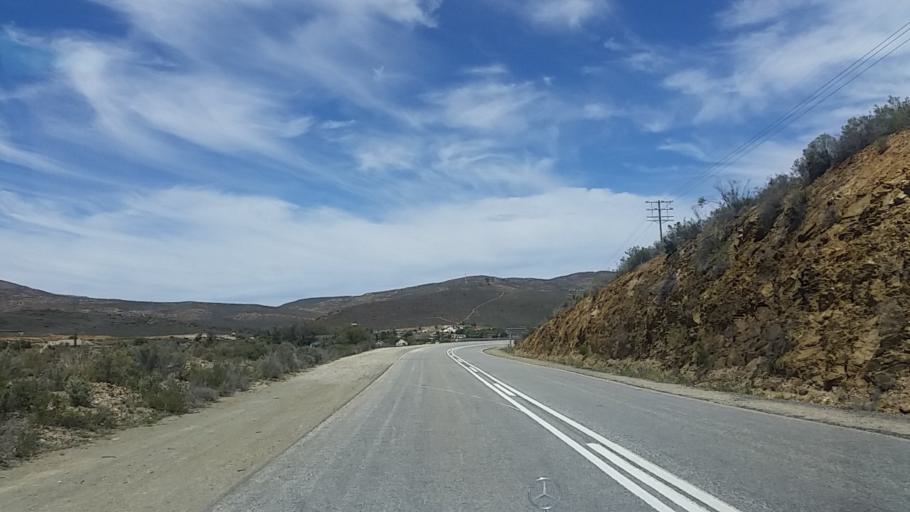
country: ZA
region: Western Cape
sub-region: Eden District Municipality
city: Knysna
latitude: -33.6437
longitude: 23.1331
